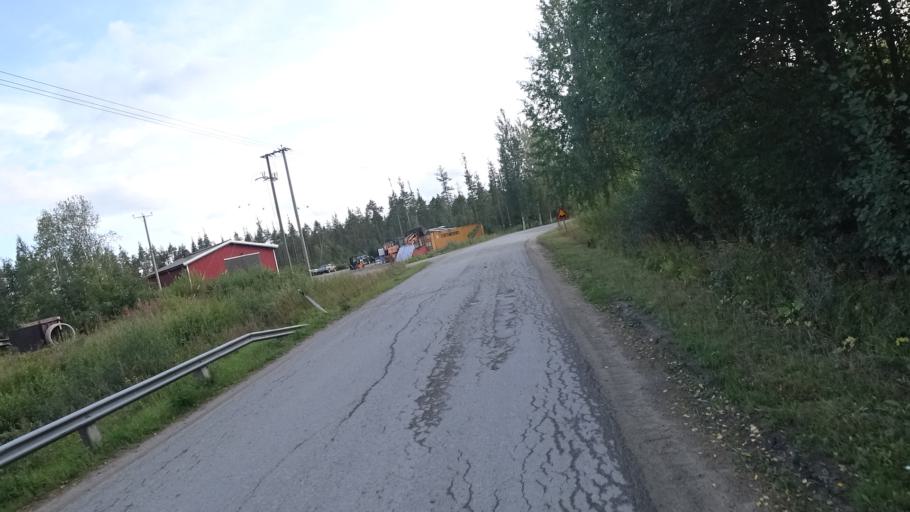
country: FI
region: North Karelia
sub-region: Joensuu
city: Ilomantsi
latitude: 62.6693
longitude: 30.9529
